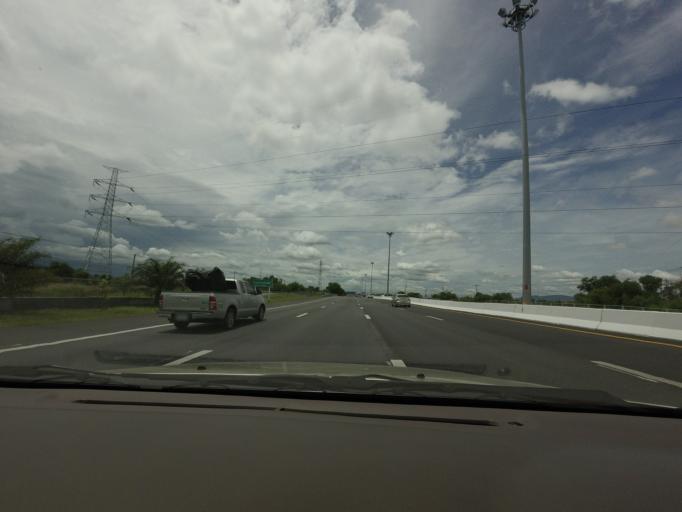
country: TH
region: Chachoengsao
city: Bang Pakong
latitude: 13.5091
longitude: 101.0344
